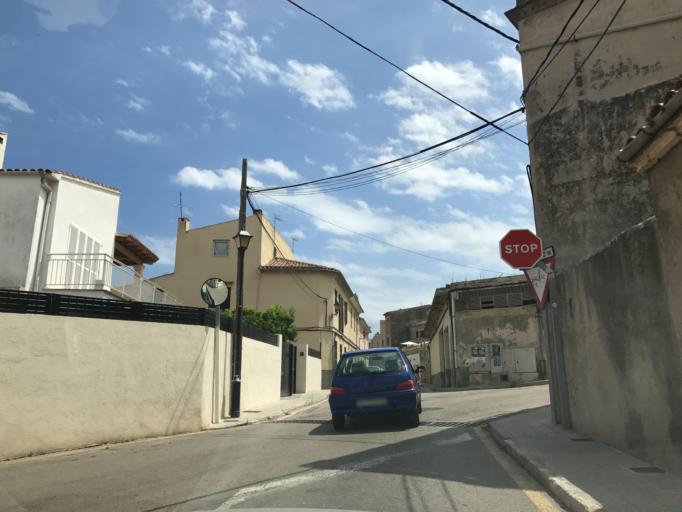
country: ES
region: Balearic Islands
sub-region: Illes Balears
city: Son Servera
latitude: 39.6250
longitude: 3.3570
